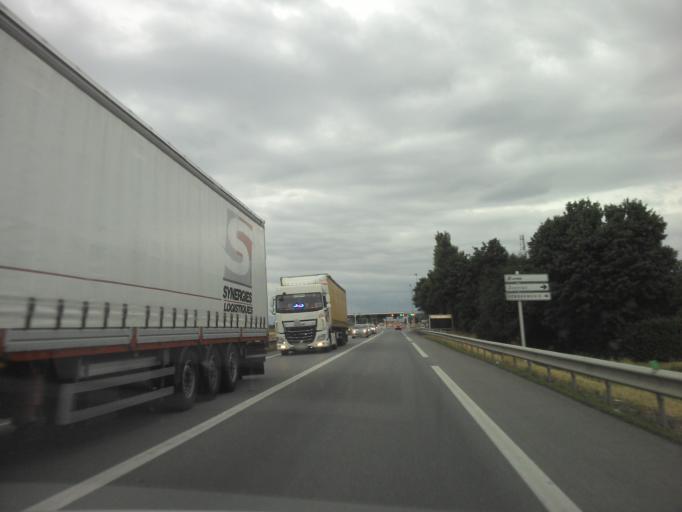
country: FR
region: Auvergne
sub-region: Departement du Puy-de-Dome
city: Riom
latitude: 45.8957
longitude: 3.1447
